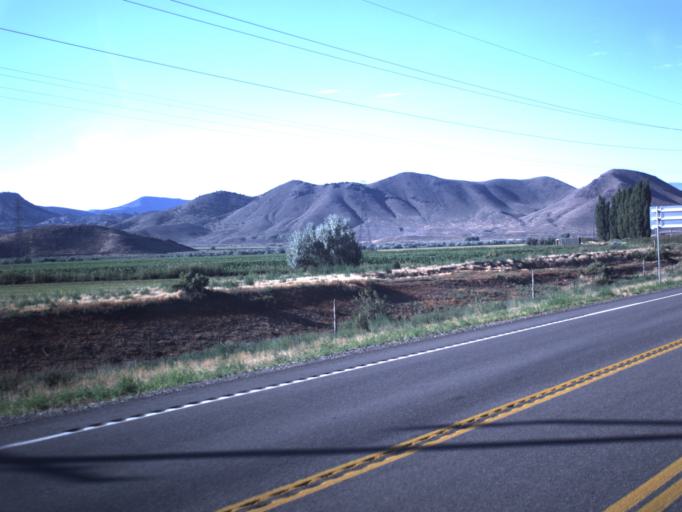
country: US
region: Utah
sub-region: Sevier County
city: Aurora
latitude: 38.9035
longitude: -111.9401
